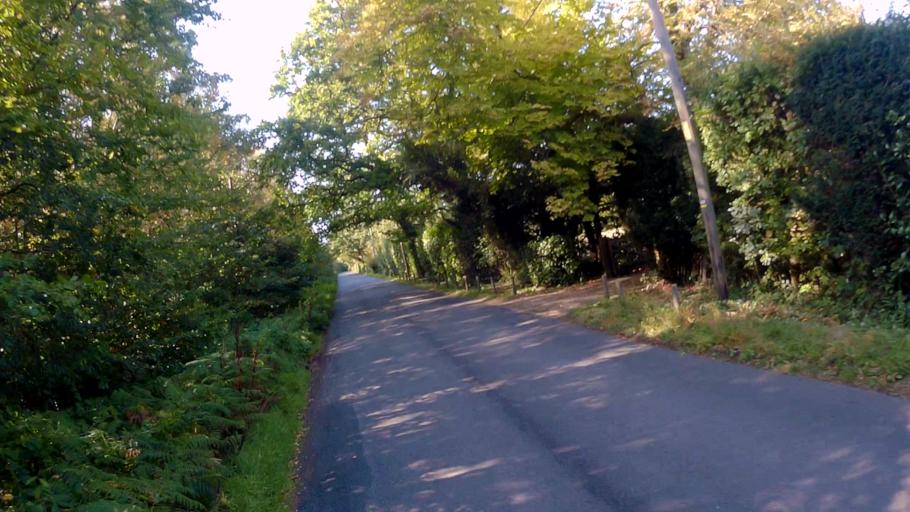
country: GB
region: England
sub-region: Hampshire
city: Lindford
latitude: 51.1614
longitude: -0.8357
